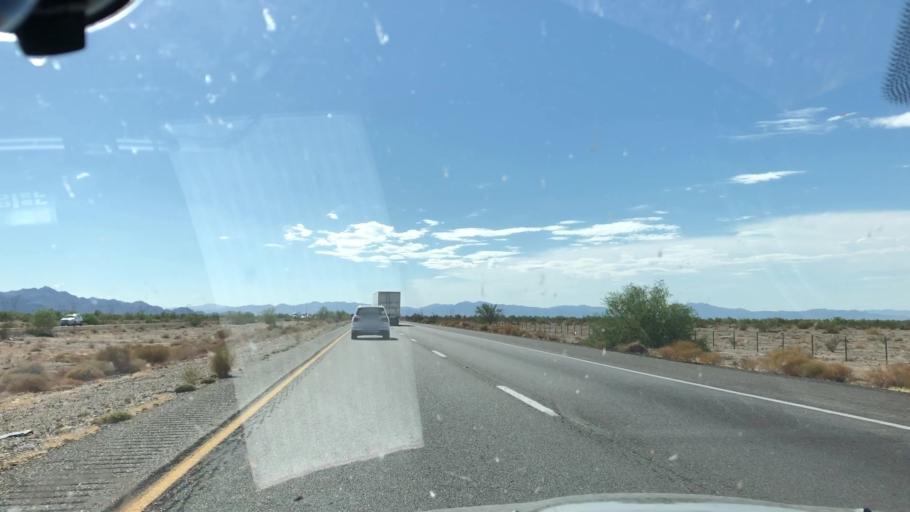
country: US
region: California
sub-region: Riverside County
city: Mesa Verde
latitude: 33.6727
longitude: -115.2101
